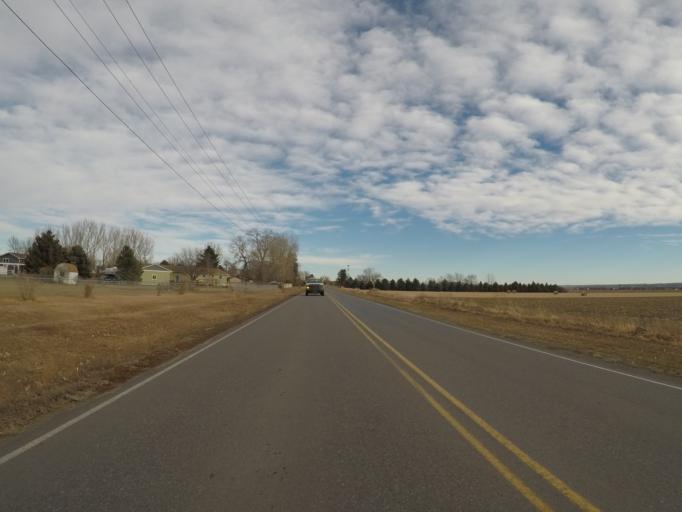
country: US
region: Montana
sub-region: Yellowstone County
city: Billings
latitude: 45.7697
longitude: -108.6448
